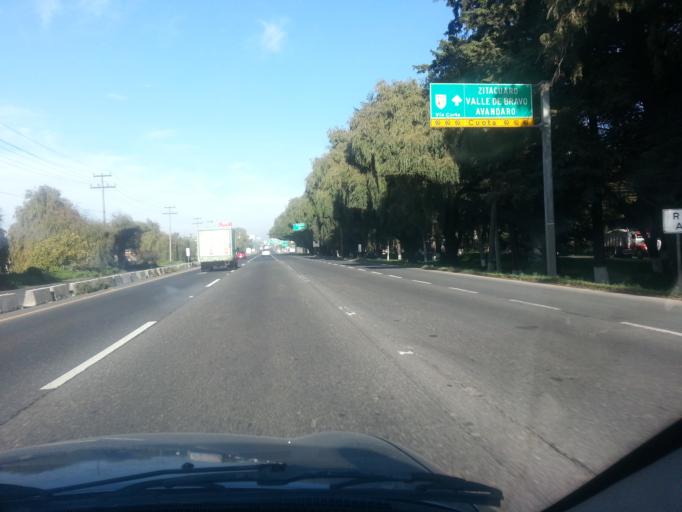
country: MX
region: Mexico
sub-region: Ocoyoacac
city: San Antonio el Llanito
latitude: 19.2848
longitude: -99.4924
